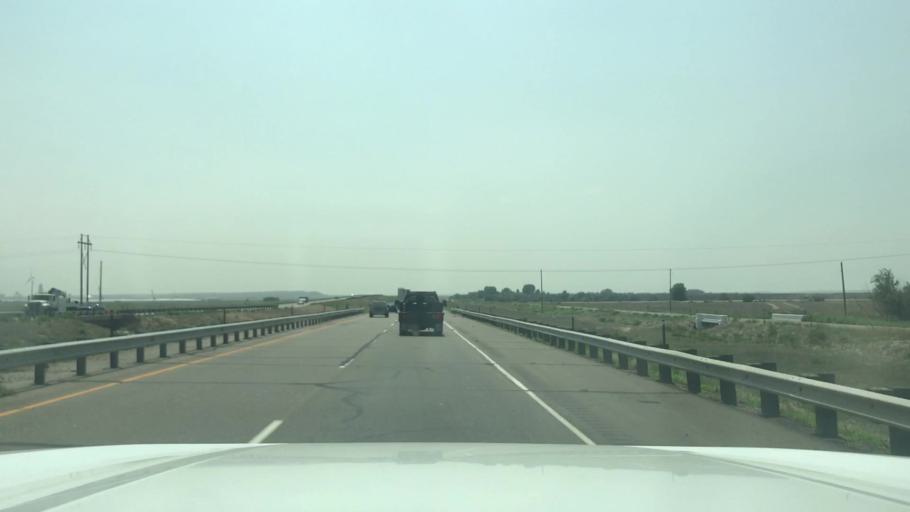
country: US
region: Colorado
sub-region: Pueblo County
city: Pueblo
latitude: 38.1906
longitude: -104.6333
